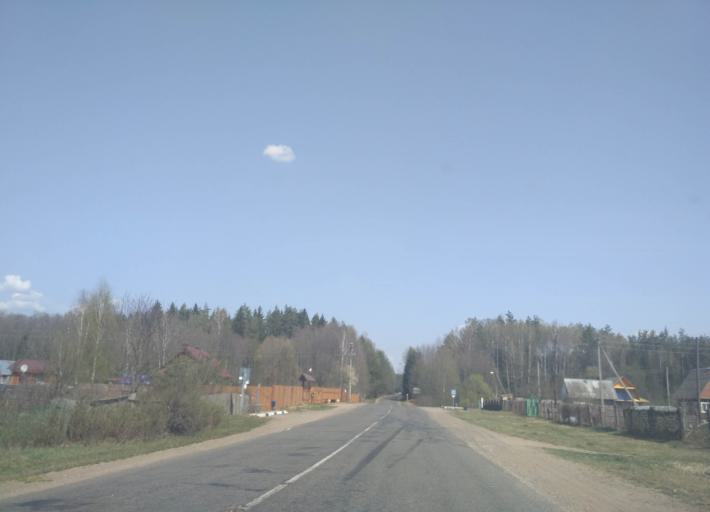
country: BY
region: Minsk
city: Loshnitsa
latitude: 54.4213
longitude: 28.6470
